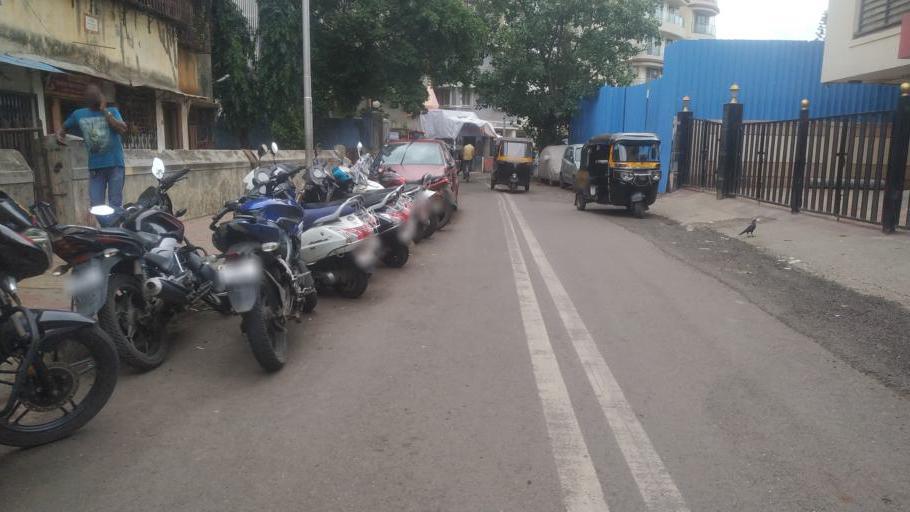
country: IN
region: Maharashtra
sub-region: Mumbai Suburban
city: Mumbai
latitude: 19.0794
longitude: 72.8681
